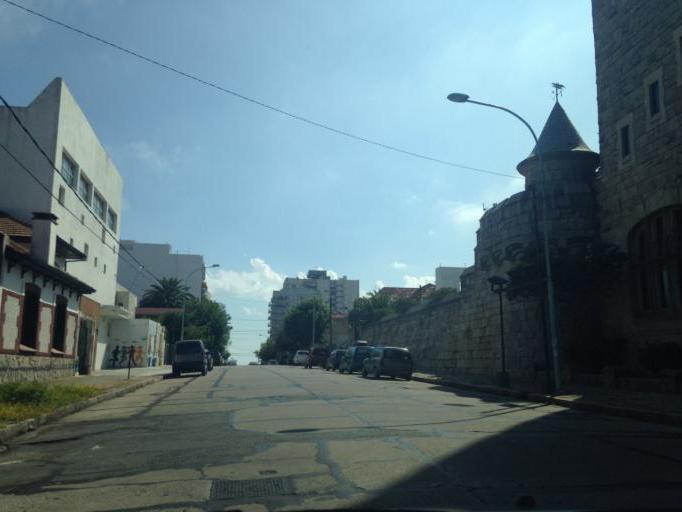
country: AR
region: Buenos Aires
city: Mar del Plata
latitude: -38.0133
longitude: -57.5355
